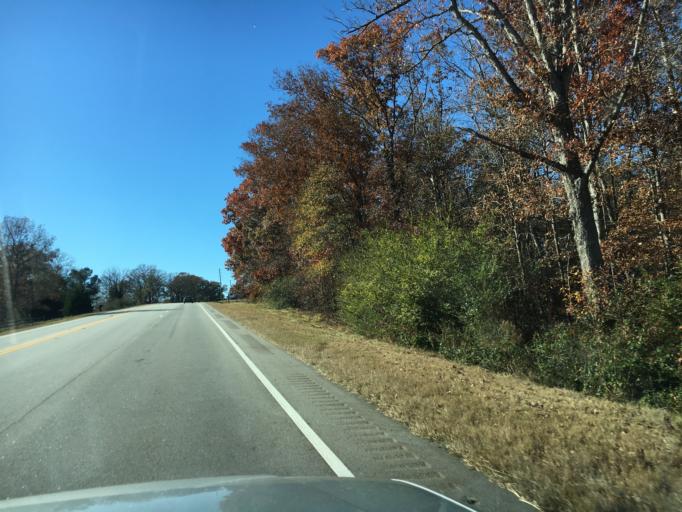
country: US
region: Georgia
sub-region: Hart County
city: Royston
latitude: 34.2932
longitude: -83.0218
